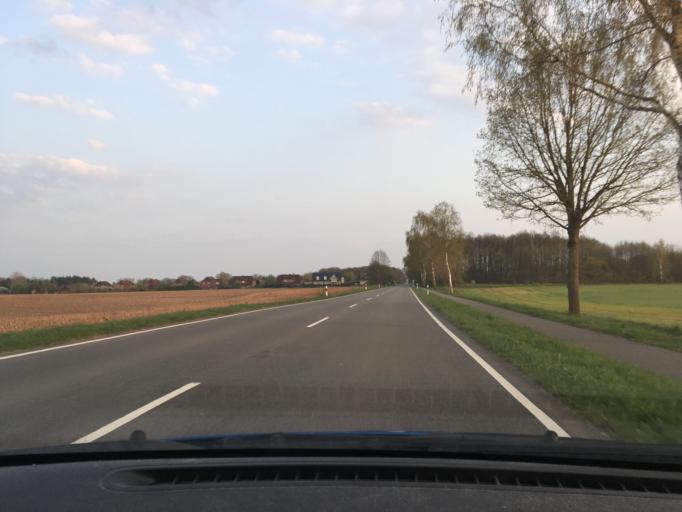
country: DE
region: Lower Saxony
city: Oldendorf
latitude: 53.1406
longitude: 10.2125
